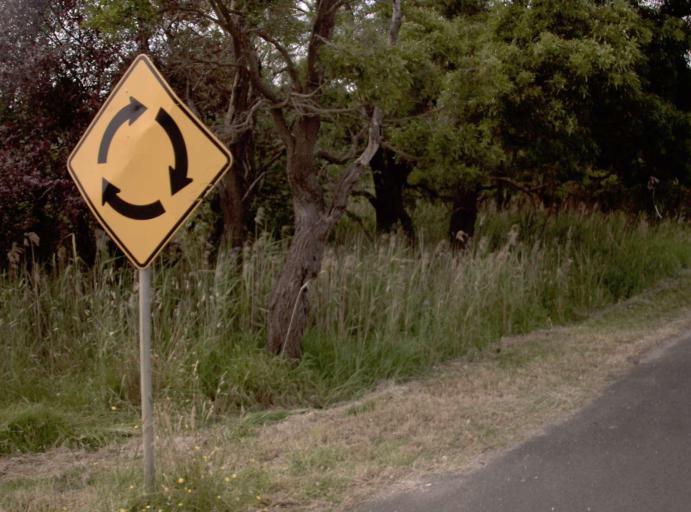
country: AU
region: Victoria
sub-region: Mornington Peninsula
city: Moorooduc
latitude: -38.2327
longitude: 145.0905
